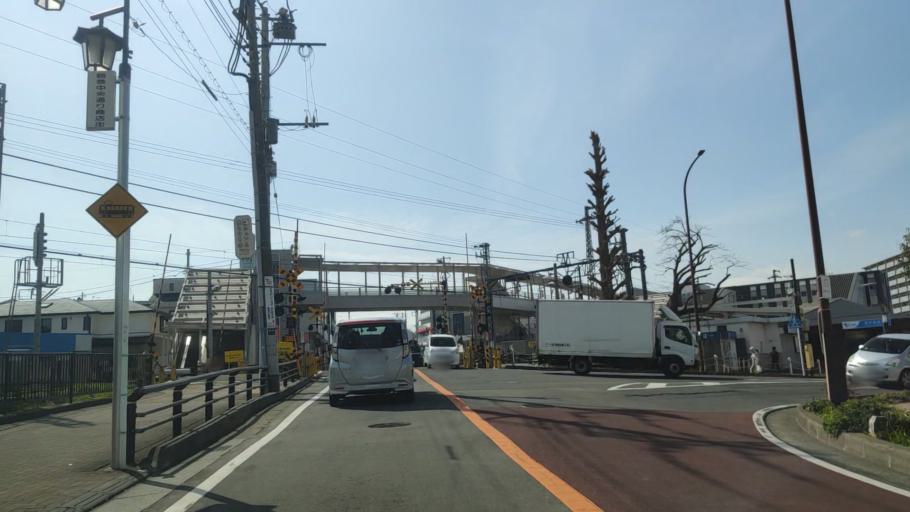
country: JP
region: Kanagawa
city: Isehara
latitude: 35.3816
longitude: 139.2785
